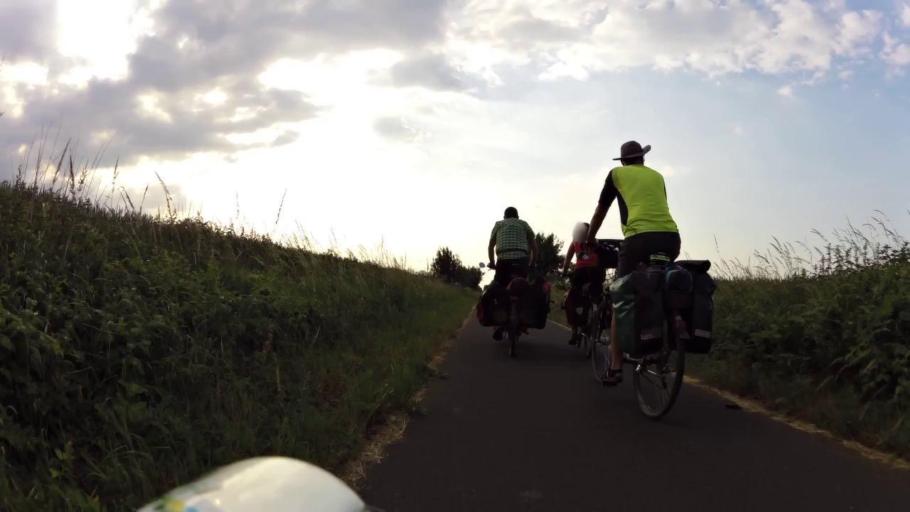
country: PL
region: Kujawsko-Pomorskie
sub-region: Powiat torunski
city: Lubianka
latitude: 53.1585
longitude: 18.4426
